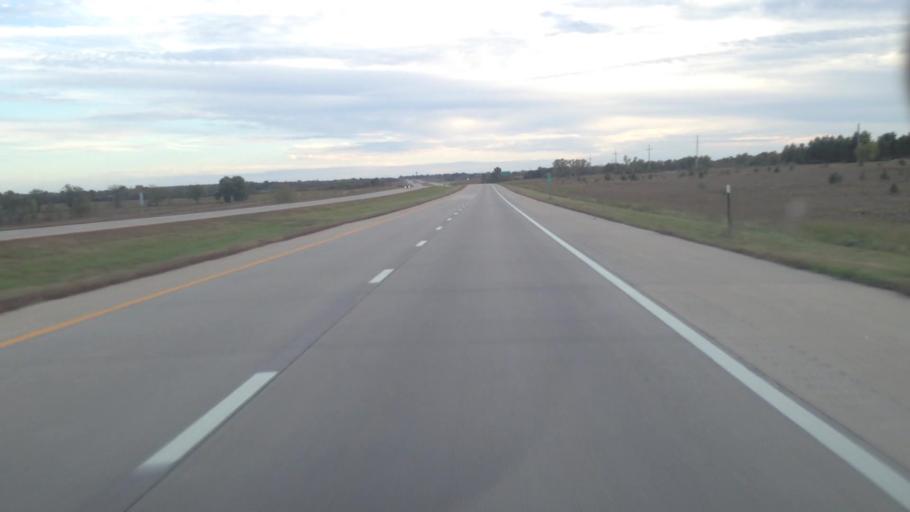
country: US
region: Kansas
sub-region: Douglas County
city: Baldwin City
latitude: 38.7351
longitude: -95.2681
